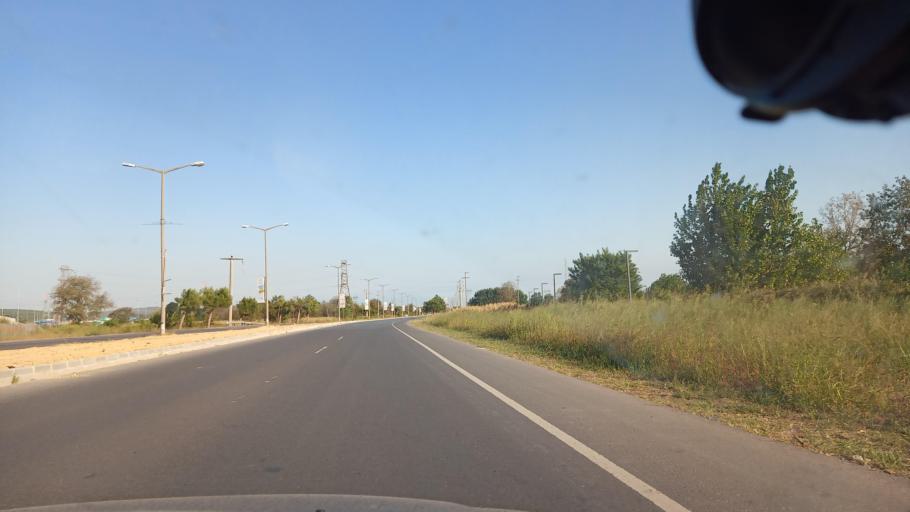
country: TR
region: Sakarya
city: Kazimpasa
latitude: 40.8436
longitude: 30.3334
